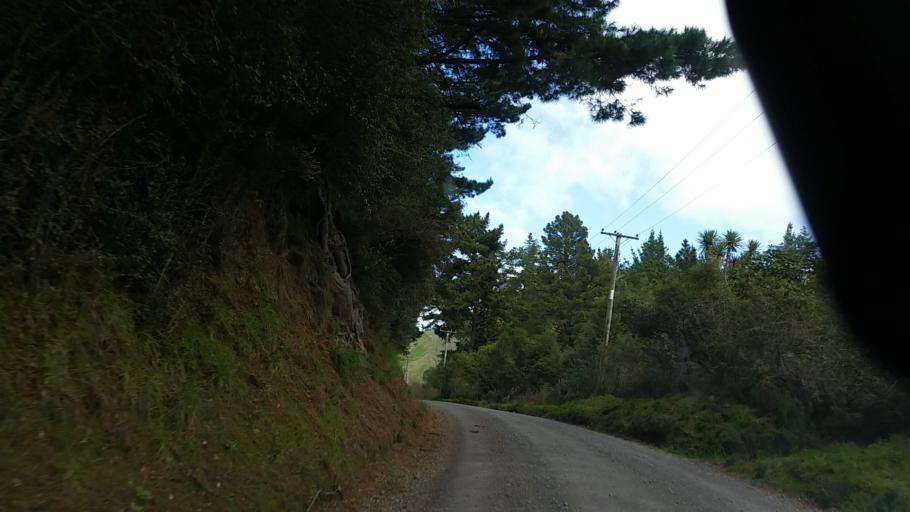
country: NZ
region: Bay of Plenty
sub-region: Rotorua District
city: Rotorua
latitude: -38.3881
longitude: 176.1704
